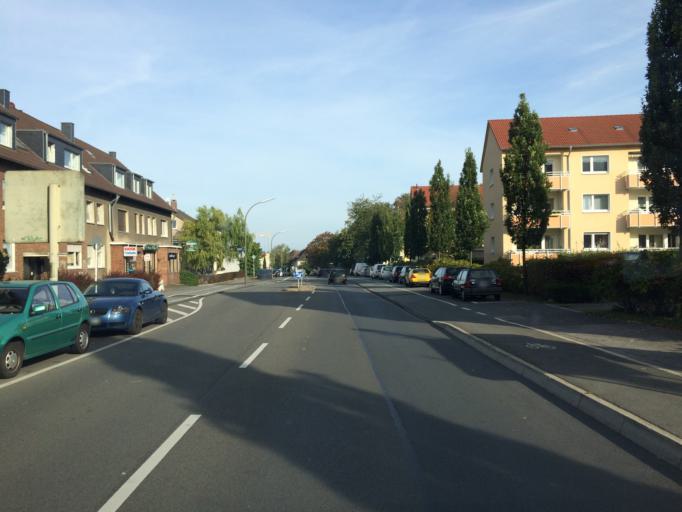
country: DE
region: North Rhine-Westphalia
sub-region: Regierungsbezirk Arnsberg
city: Dortmund
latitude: 51.4828
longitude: 7.4388
